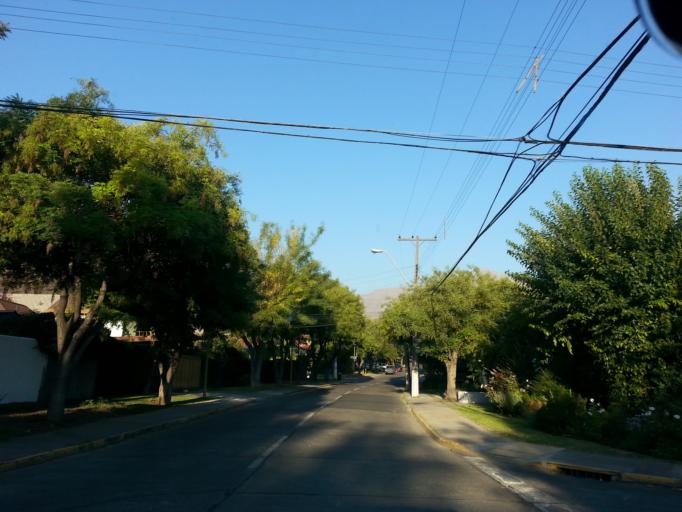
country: CL
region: Santiago Metropolitan
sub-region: Provincia de Santiago
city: Villa Presidente Frei, Nunoa, Santiago, Chile
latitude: -33.4029
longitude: -70.5425
